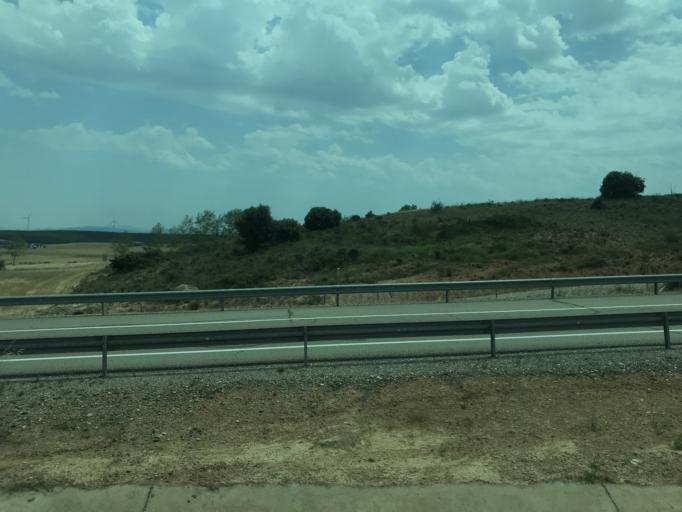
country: ES
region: Castille and Leon
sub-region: Provincia de Burgos
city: Cogollos
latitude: 42.1929
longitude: -3.6976
